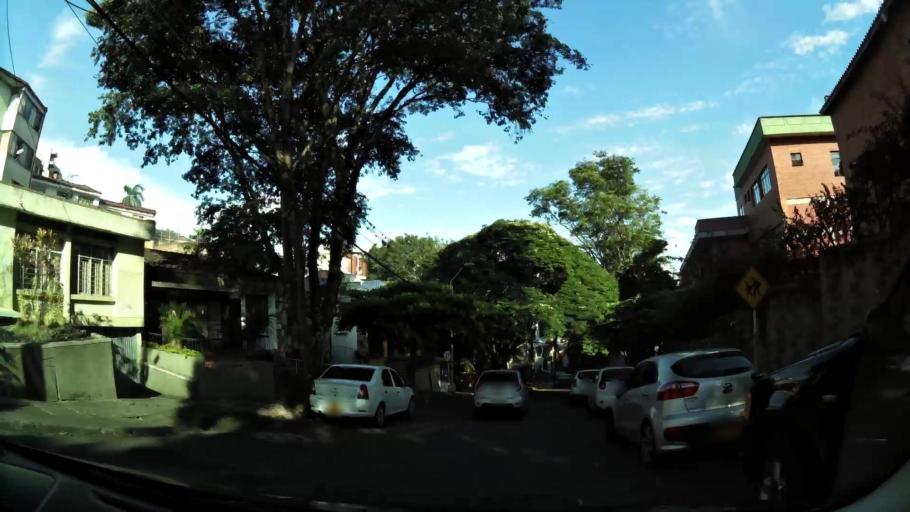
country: CO
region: Valle del Cauca
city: Cali
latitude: 3.4271
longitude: -76.5496
